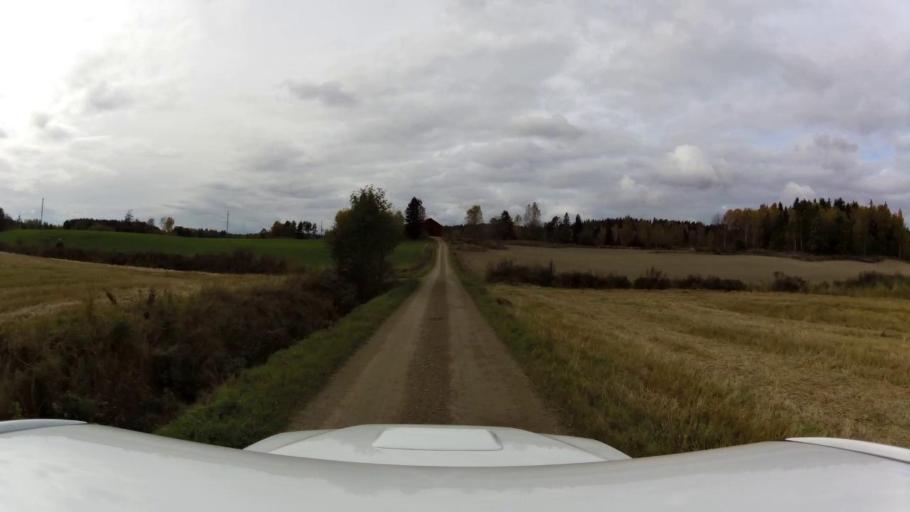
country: SE
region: OEstergoetland
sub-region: Linkopings Kommun
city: Ekangen
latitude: 58.5632
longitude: 15.6657
